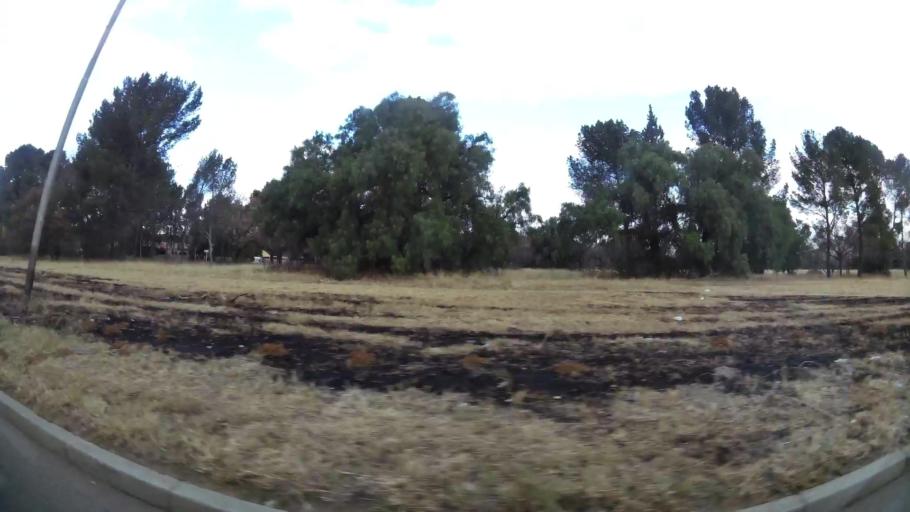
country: ZA
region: Orange Free State
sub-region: Lejweleputswa District Municipality
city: Welkom
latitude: -27.9954
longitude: 26.7172
